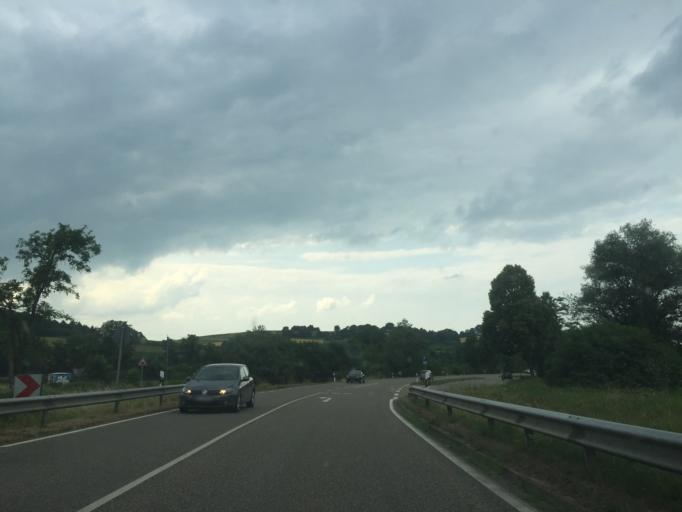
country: DE
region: Baden-Wuerttemberg
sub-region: Karlsruhe Region
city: Zuzenhausen
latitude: 49.2827
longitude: 8.8270
